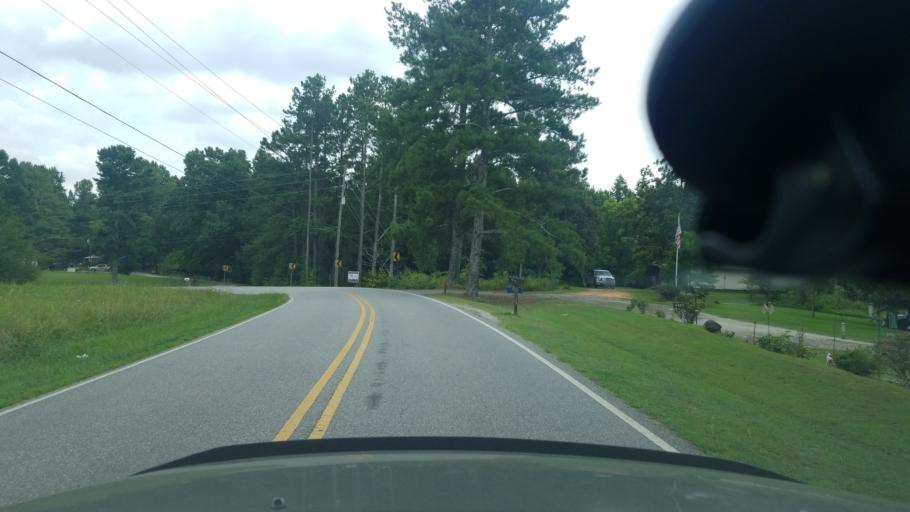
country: US
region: Georgia
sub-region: Forsyth County
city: Cumming
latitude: 34.3158
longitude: -84.1715
